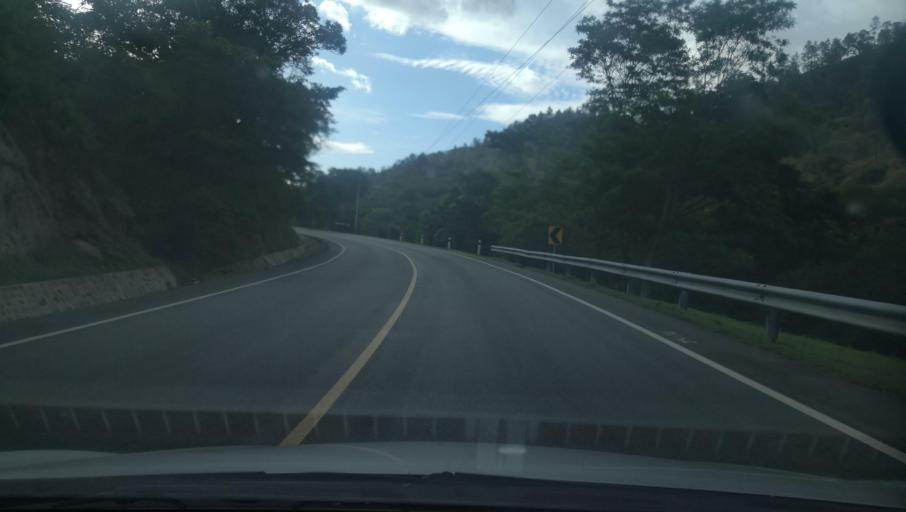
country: NI
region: Nueva Segovia
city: Mozonte
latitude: 13.6984
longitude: -86.4880
